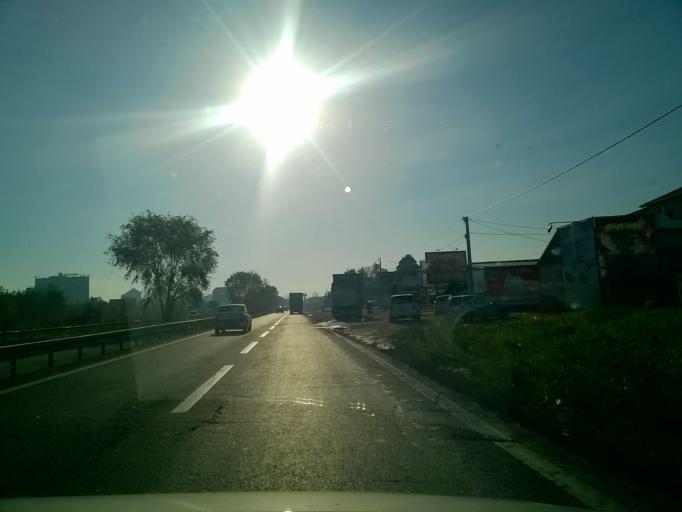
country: RS
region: Central Serbia
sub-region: Belgrade
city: Zemun
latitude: 44.8599
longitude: 20.3555
